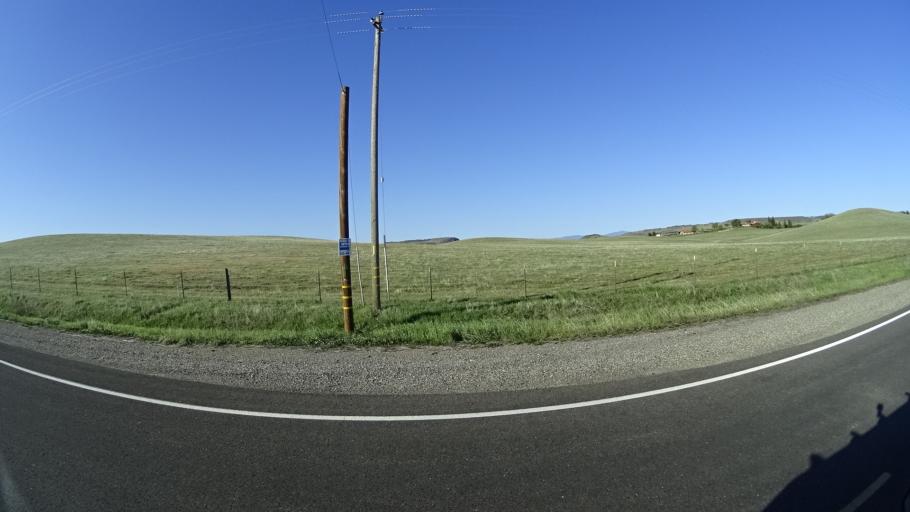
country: US
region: California
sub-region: Glenn County
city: Orland
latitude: 39.7841
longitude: -122.2980
